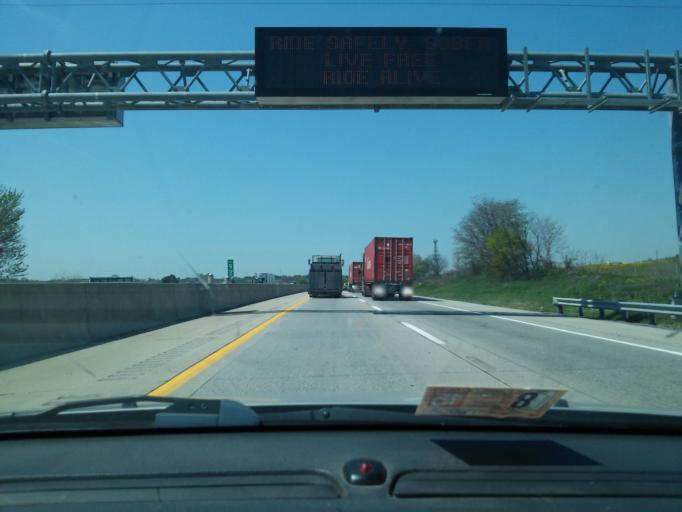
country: US
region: Pennsylvania
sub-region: Lebanon County
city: Fredericksburg
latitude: 40.4634
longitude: -76.3527
